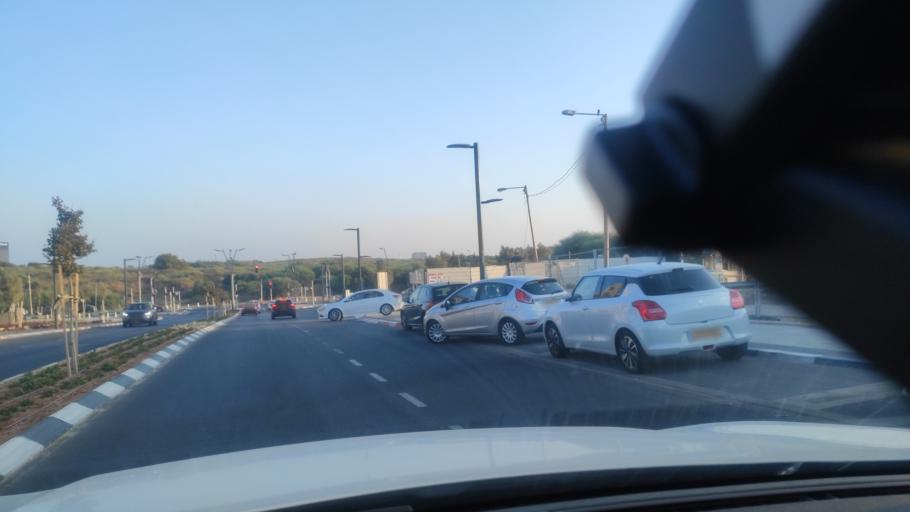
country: IL
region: Tel Aviv
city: Herzliya Pituah
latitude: 32.1651
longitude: 34.8028
